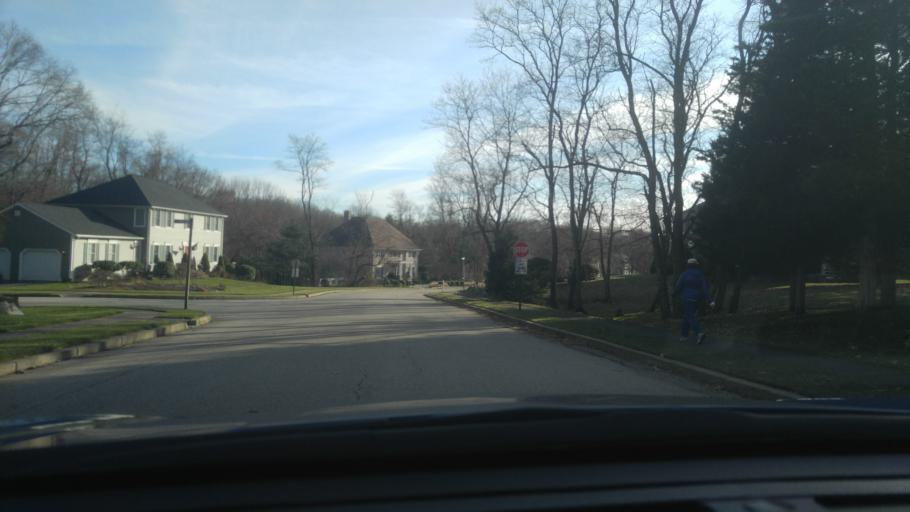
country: US
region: Rhode Island
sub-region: Kent County
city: East Greenwich
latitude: 41.6783
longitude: -71.4696
